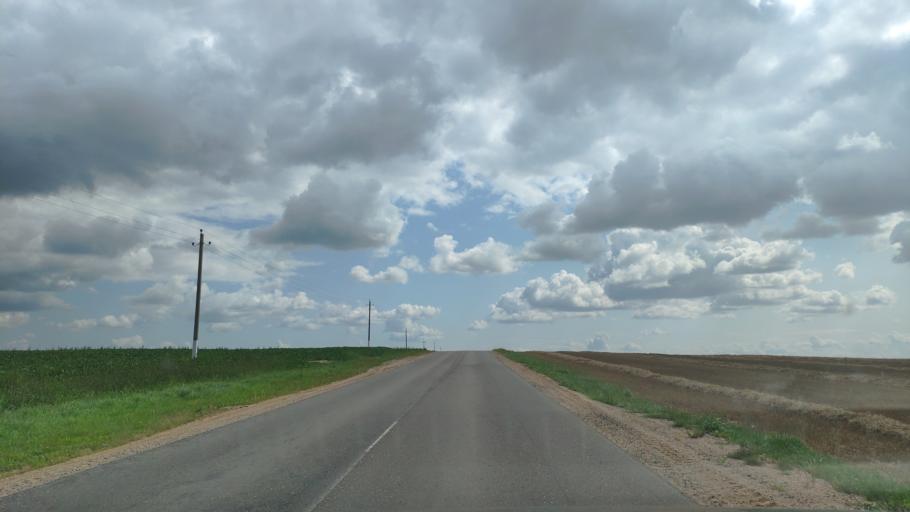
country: BY
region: Minsk
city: Khatsyezhyna
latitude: 53.8500
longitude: 27.3109
